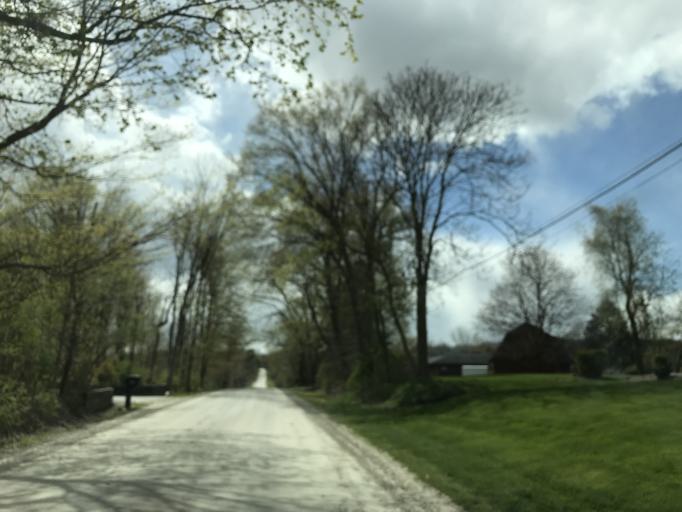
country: US
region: Michigan
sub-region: Oakland County
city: South Lyon
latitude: 42.3771
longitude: -83.5865
